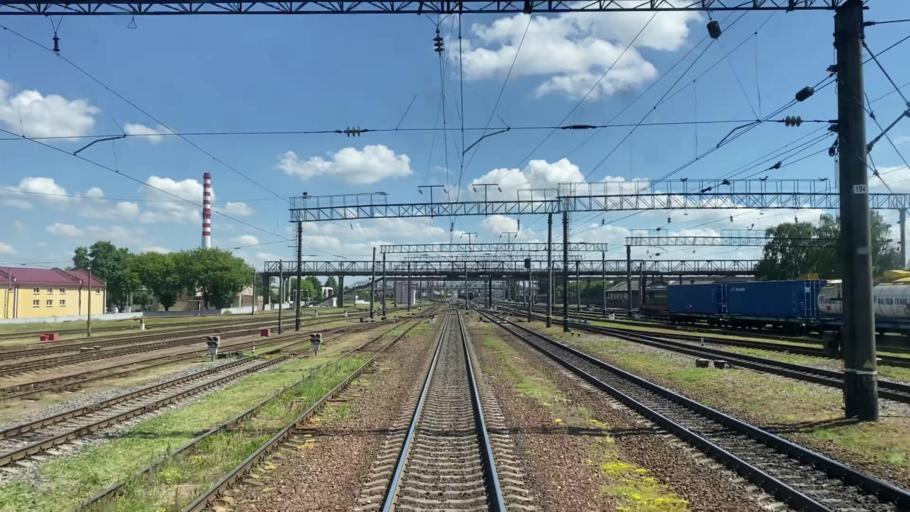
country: BY
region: Brest
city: Baranovichi
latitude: 53.1357
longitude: 26.0020
